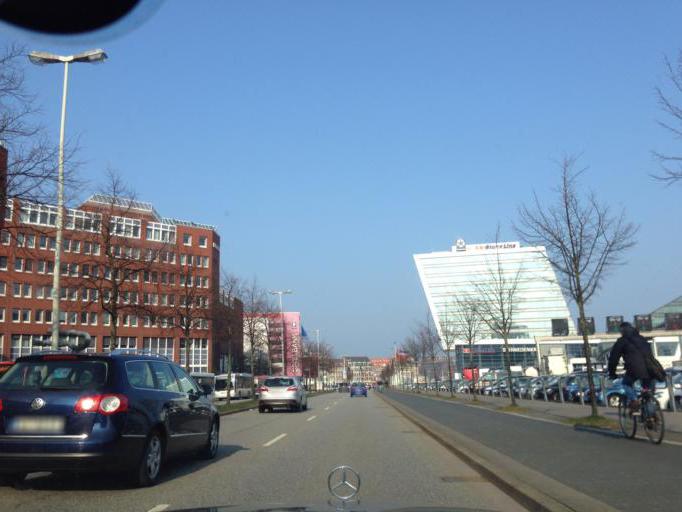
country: DE
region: Schleswig-Holstein
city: Kiel
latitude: 54.3187
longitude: 10.1361
